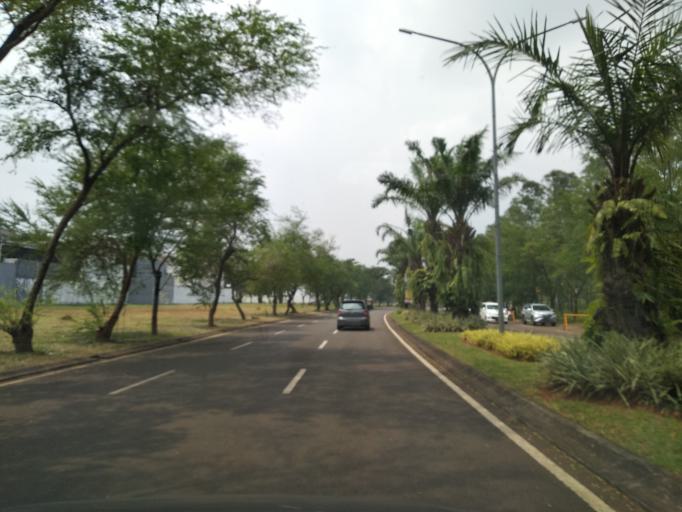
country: ID
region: West Java
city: Bekasi
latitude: -6.2950
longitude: 107.0493
